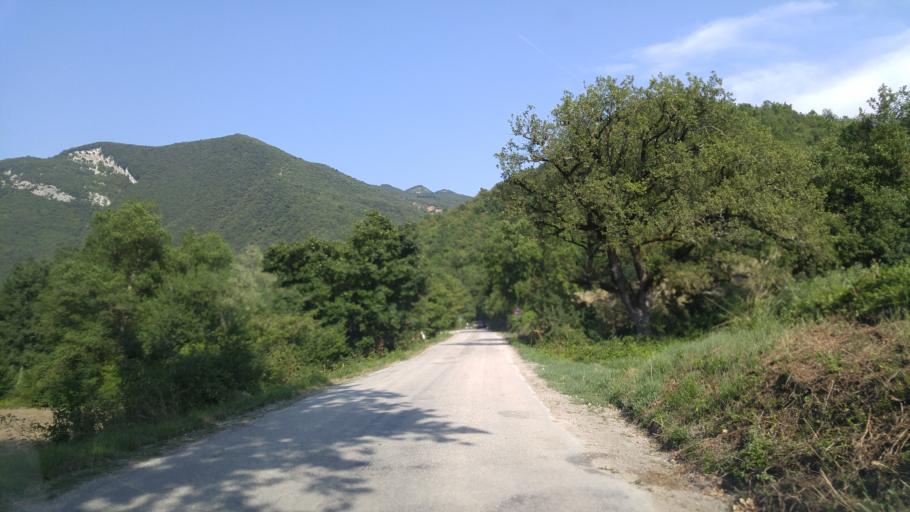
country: IT
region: The Marches
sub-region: Provincia di Pesaro e Urbino
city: Acqualagna
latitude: 43.6337
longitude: 12.7020
